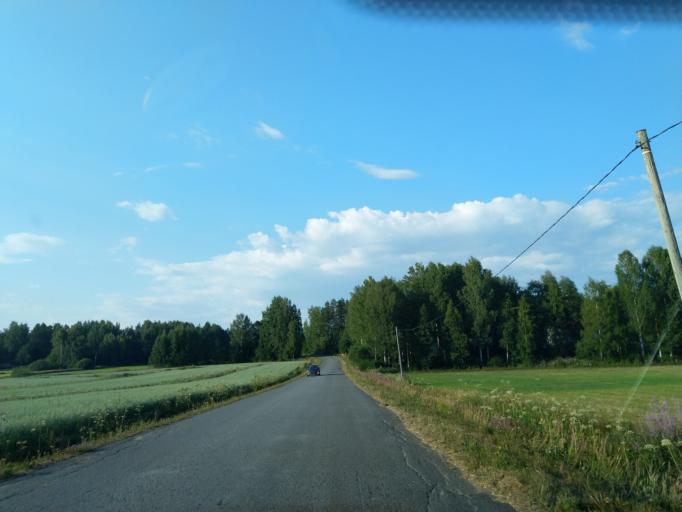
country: FI
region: Satakunta
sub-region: Pohjois-Satakunta
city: Honkajoki
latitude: 61.8159
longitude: 22.1984
